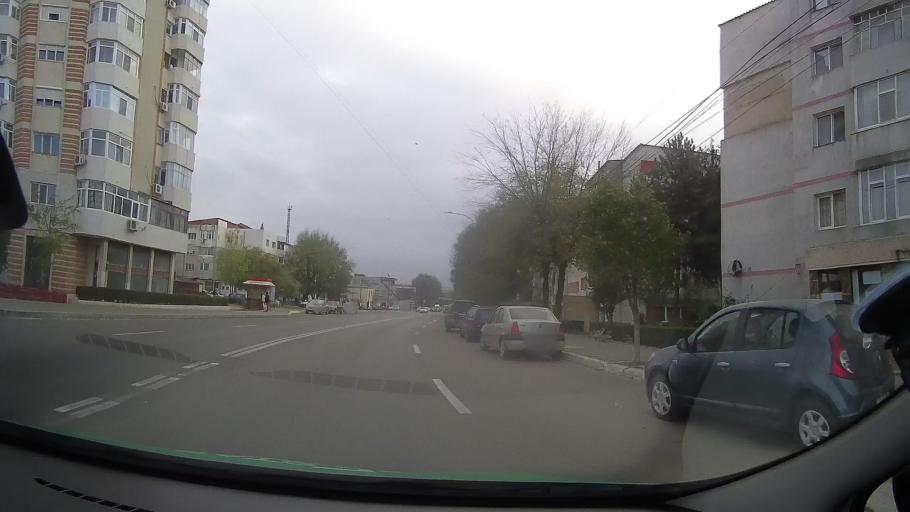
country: RO
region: Constanta
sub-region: Municipiul Medgidia
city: Medgidia
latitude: 44.2615
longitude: 28.2625
